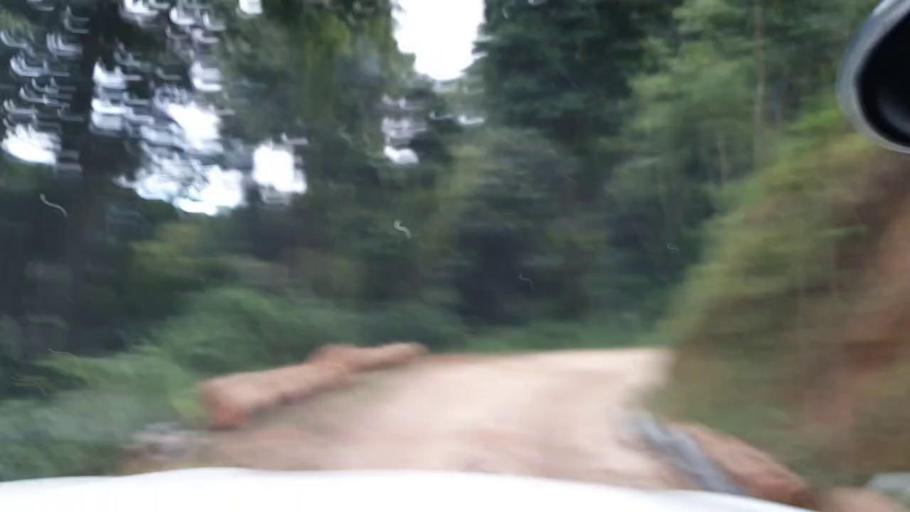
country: RW
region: Southern Province
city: Nzega
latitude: -2.5529
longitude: 29.2371
